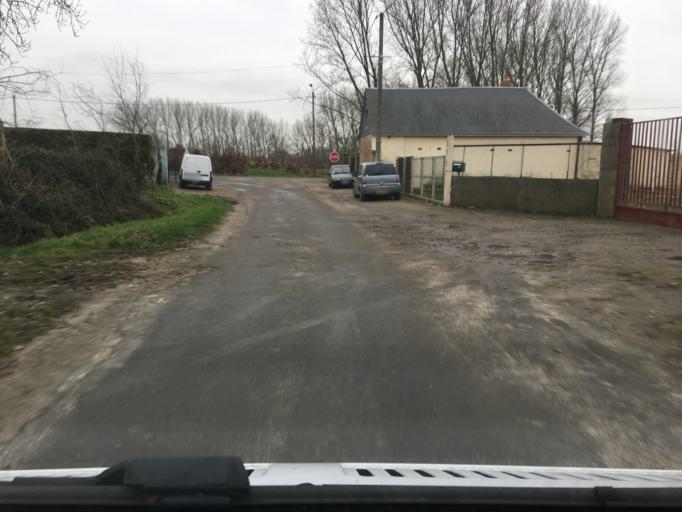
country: FR
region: Picardie
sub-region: Departement de la Somme
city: Pende
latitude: 50.1727
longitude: 1.5456
